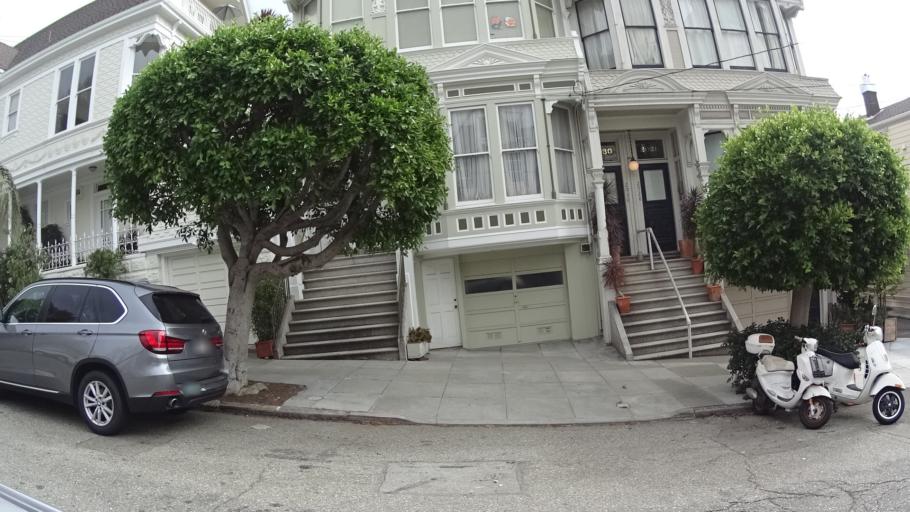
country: US
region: California
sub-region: San Francisco County
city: San Francisco
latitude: 37.7891
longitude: -122.4373
